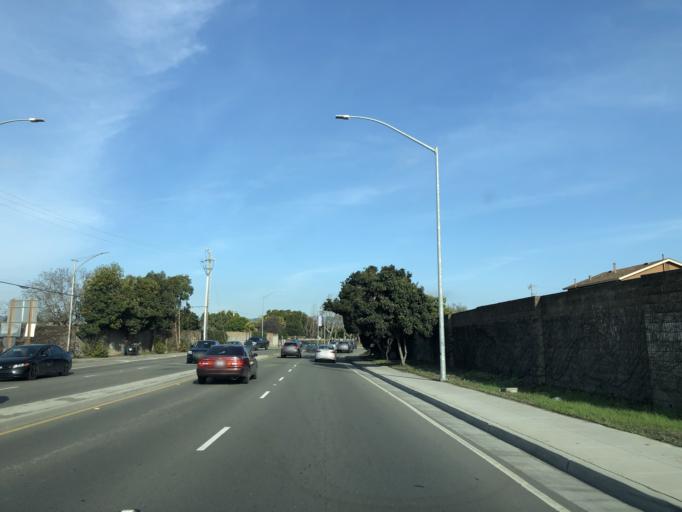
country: US
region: California
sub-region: Alameda County
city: San Leandro
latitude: 37.7198
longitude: -122.1743
